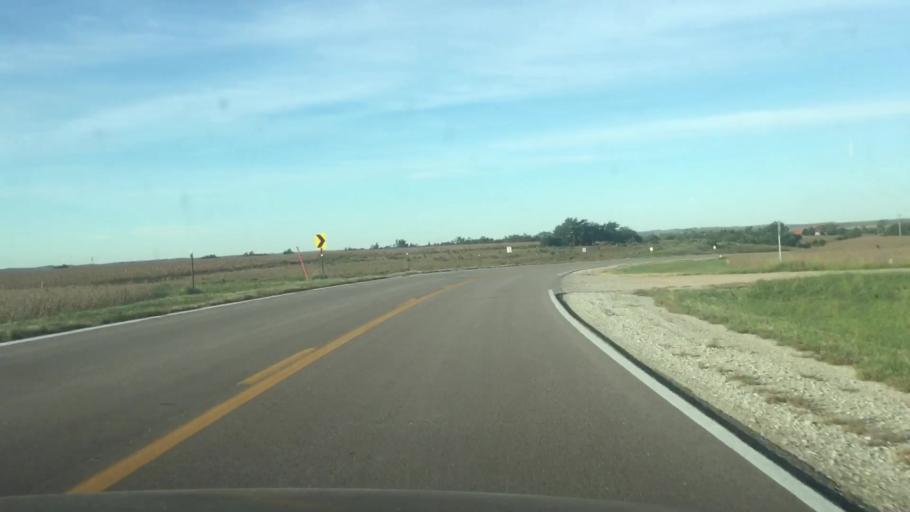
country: US
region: Nebraska
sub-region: Jefferson County
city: Fairbury
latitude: 40.0418
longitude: -97.0104
